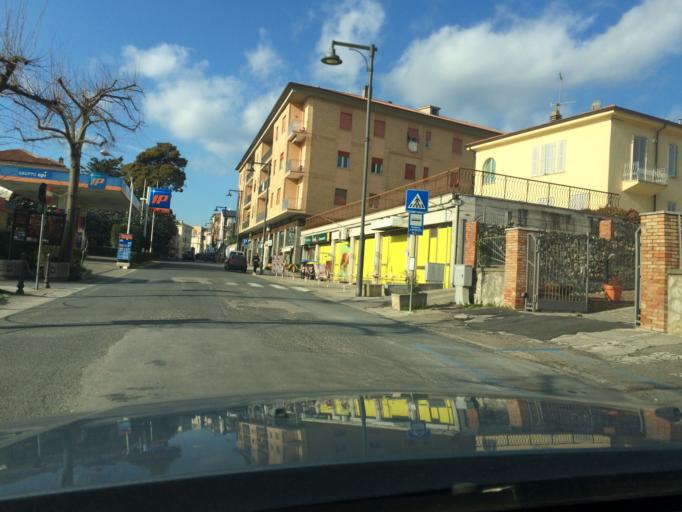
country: IT
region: Umbria
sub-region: Provincia di Terni
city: Amelia
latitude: 42.5521
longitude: 12.4195
